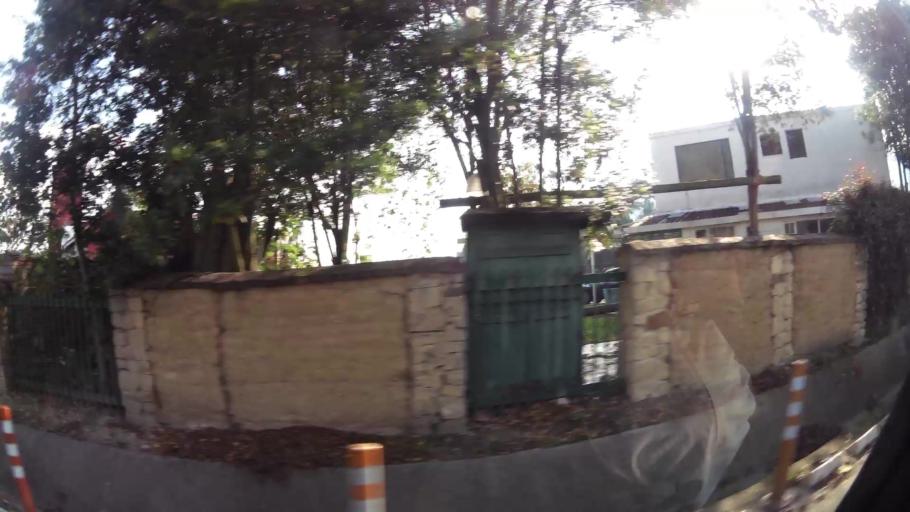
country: CO
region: Cundinamarca
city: Cota
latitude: 4.8049
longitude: -74.1101
